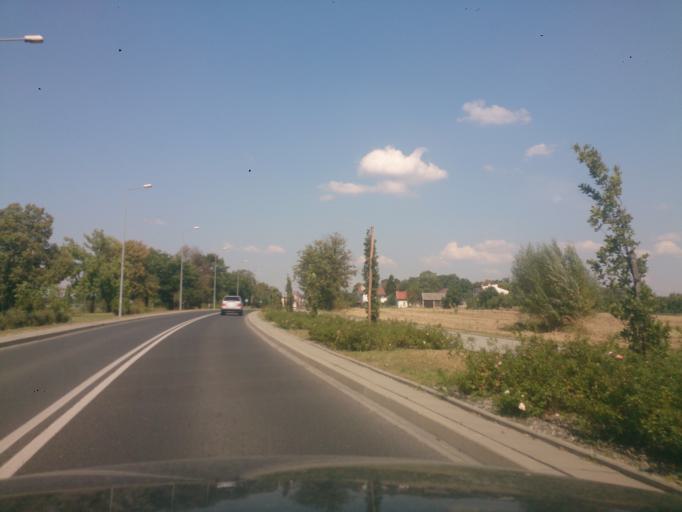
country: PL
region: Subcarpathian Voivodeship
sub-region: Powiat rzeszowski
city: Glogow Malopolski
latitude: 50.1446
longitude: 21.9635
